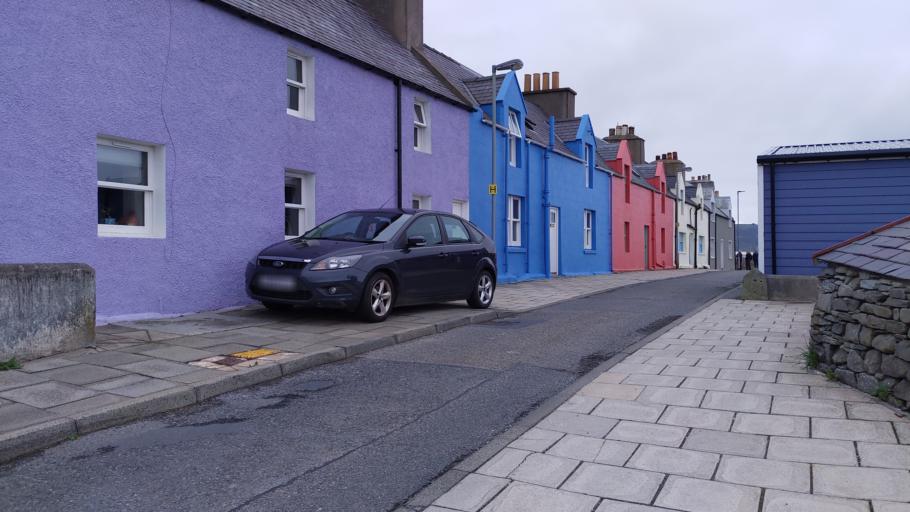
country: GB
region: Scotland
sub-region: Shetland Islands
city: Lerwick
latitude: 60.1365
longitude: -1.2751
